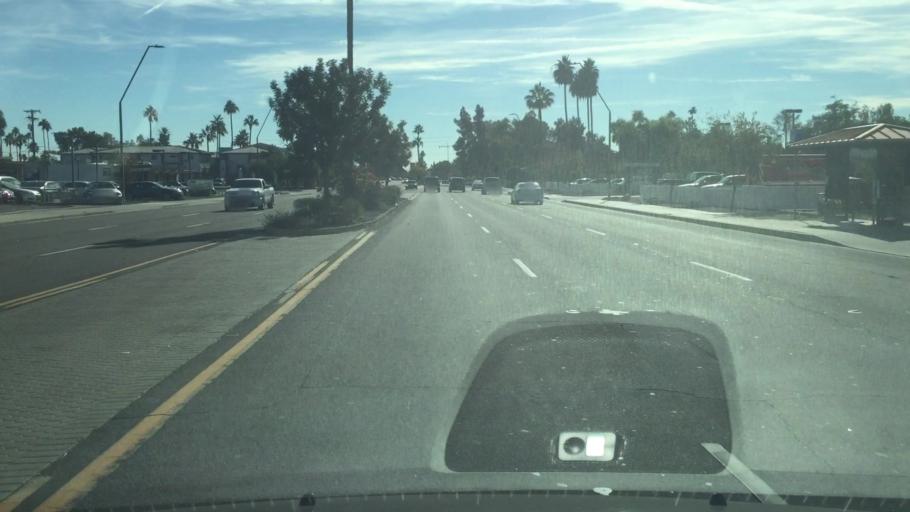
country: US
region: Arizona
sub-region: Maricopa County
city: Tempe
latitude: 33.4545
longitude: -111.9265
